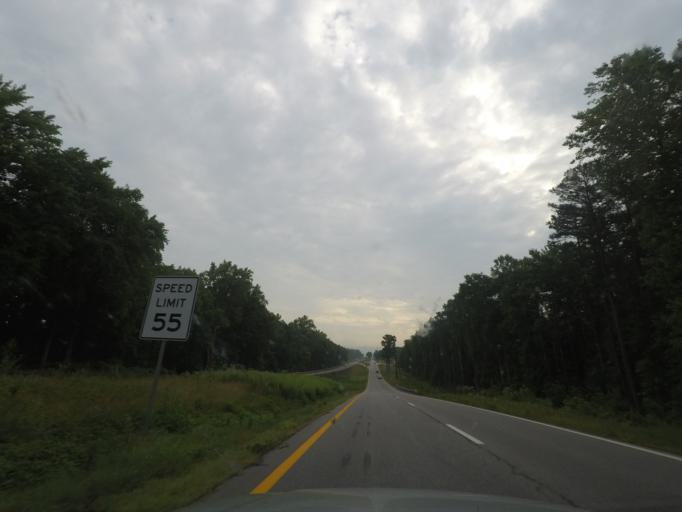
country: US
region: Virginia
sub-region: Mecklenburg County
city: Chase City
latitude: 36.9003
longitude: -78.5385
